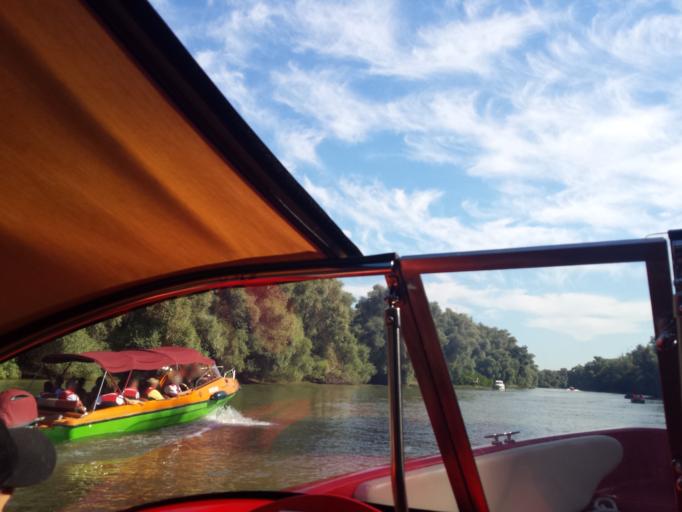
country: RO
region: Tulcea
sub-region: Comuna Nufaru
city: Nufaru
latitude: 45.2218
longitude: 28.8812
